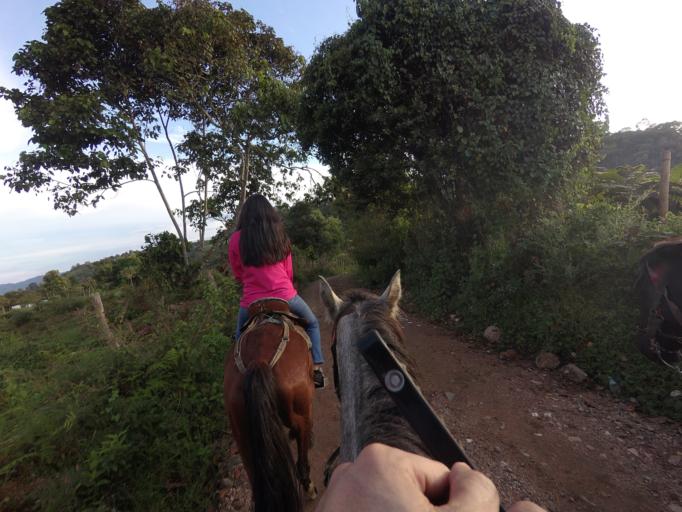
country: CO
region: Huila
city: San Agustin
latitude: 1.9001
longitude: -76.2729
